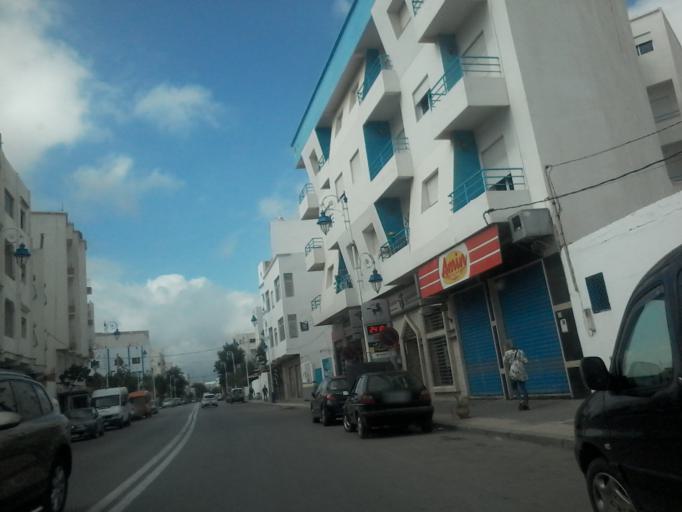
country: MA
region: Tanger-Tetouan
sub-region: Tetouan
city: Martil
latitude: 35.6259
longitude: -5.2762
